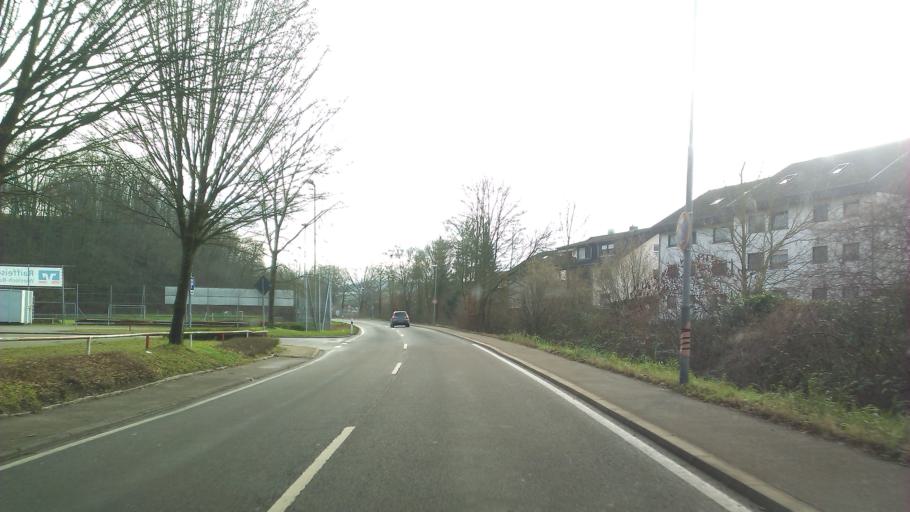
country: DE
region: Baden-Wuerttemberg
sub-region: Karlsruhe Region
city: Horrenberg
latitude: 49.2780
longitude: 8.7828
